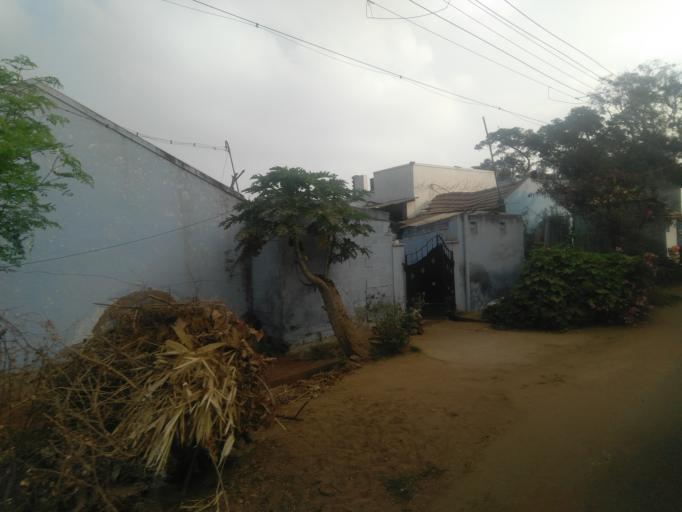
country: IN
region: Tamil Nadu
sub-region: Coimbatore
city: Coimbatore
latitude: 11.0558
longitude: 76.9028
